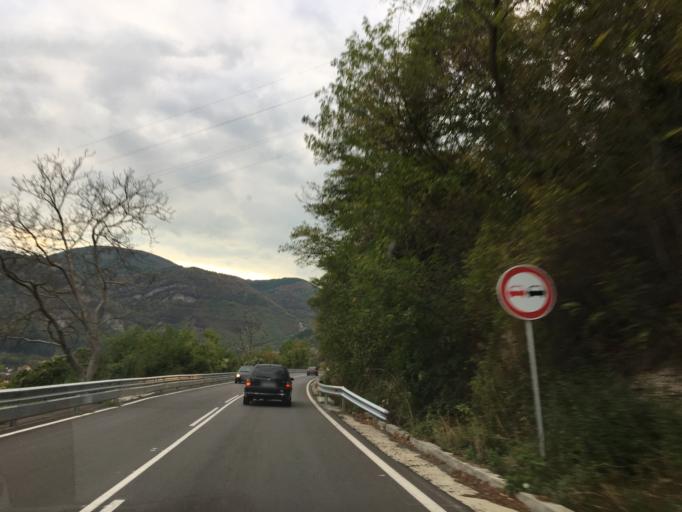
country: BG
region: Sofiya
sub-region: Obshtina Svoge
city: Bov
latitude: 43.0116
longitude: 23.3556
